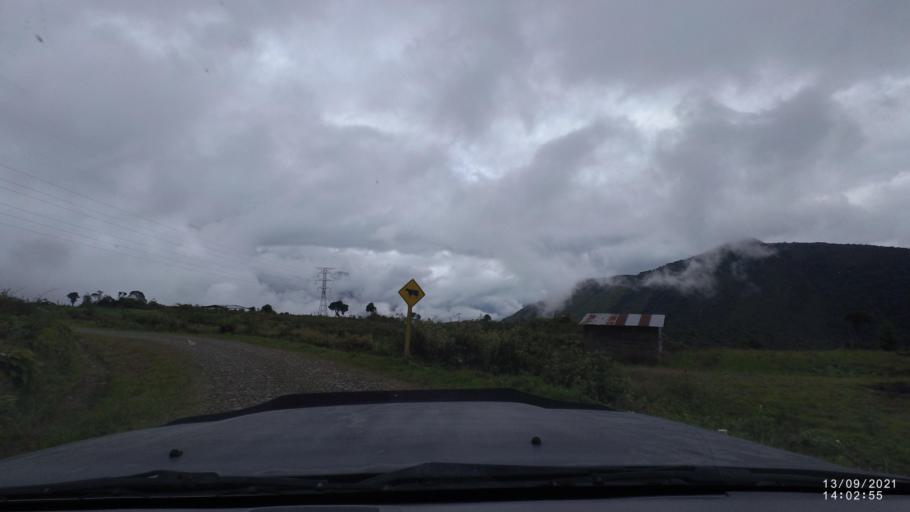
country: BO
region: Cochabamba
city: Colomi
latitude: -17.2071
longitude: -65.8664
